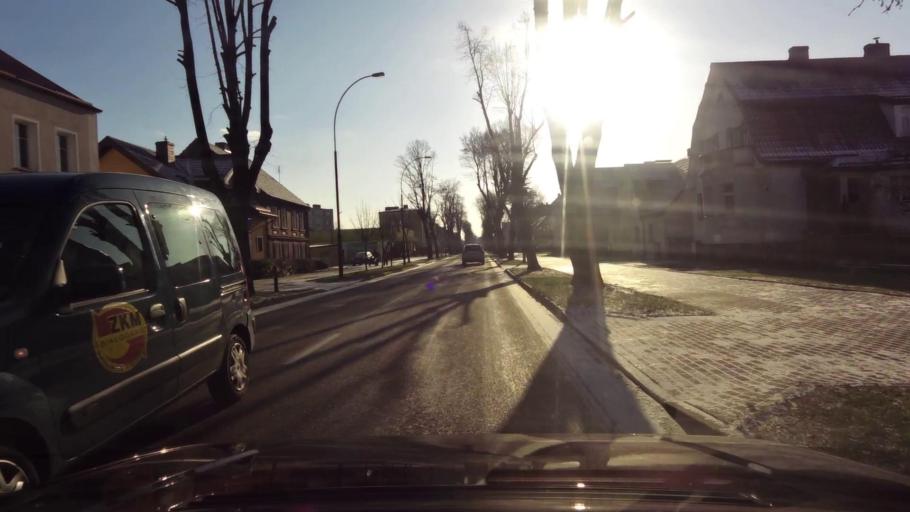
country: PL
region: West Pomeranian Voivodeship
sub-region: Powiat bialogardzki
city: Bialogard
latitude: 54.0117
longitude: 15.9815
